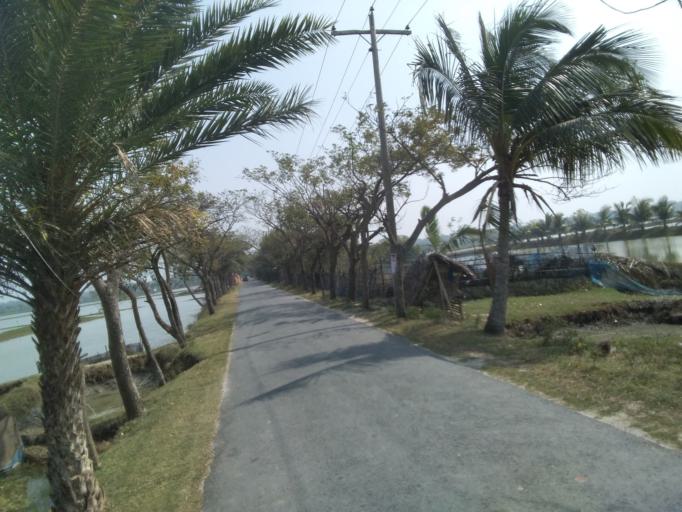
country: IN
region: West Bengal
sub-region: North 24 Parganas
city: Taki
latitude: 22.5934
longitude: 88.9858
